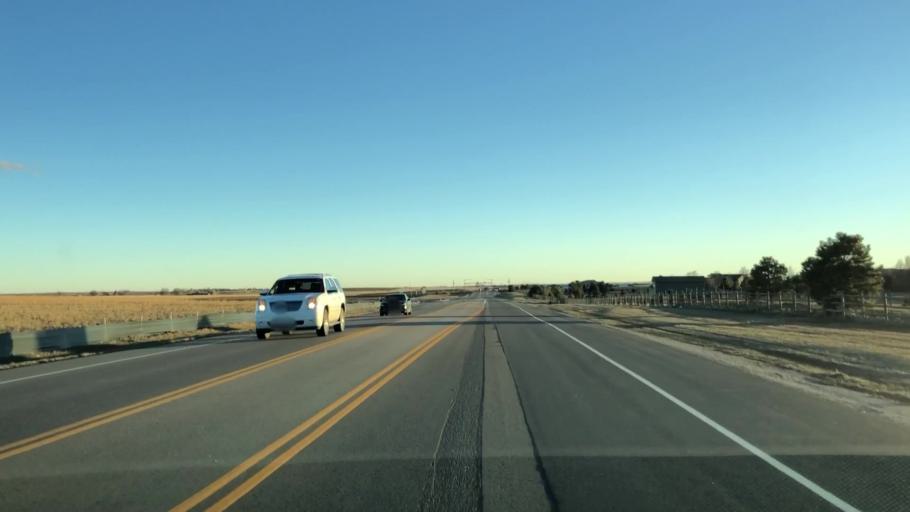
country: US
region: Colorado
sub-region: Weld County
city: Windsor
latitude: 40.4415
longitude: -104.9443
